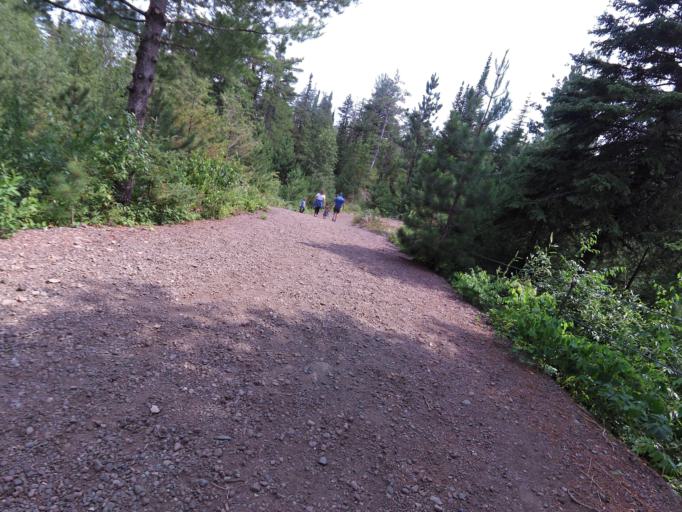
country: CA
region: Ontario
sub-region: Thunder Bay District
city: Thunder Bay
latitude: 48.8014
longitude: -88.6163
